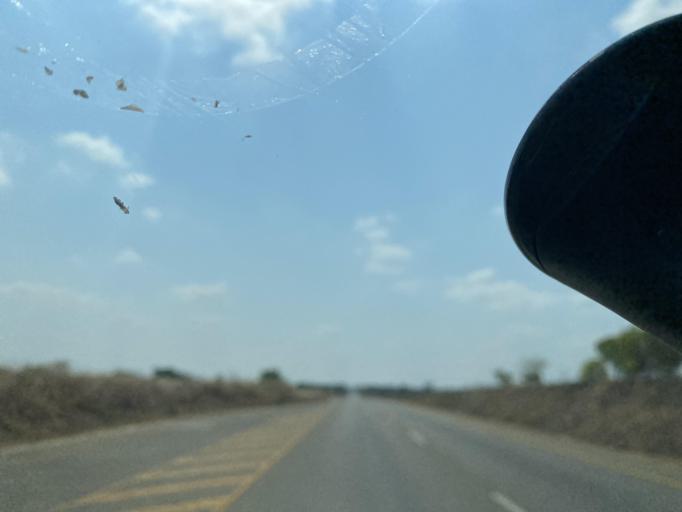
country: ZM
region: Lusaka
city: Chongwe
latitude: -15.5427
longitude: 28.6627
